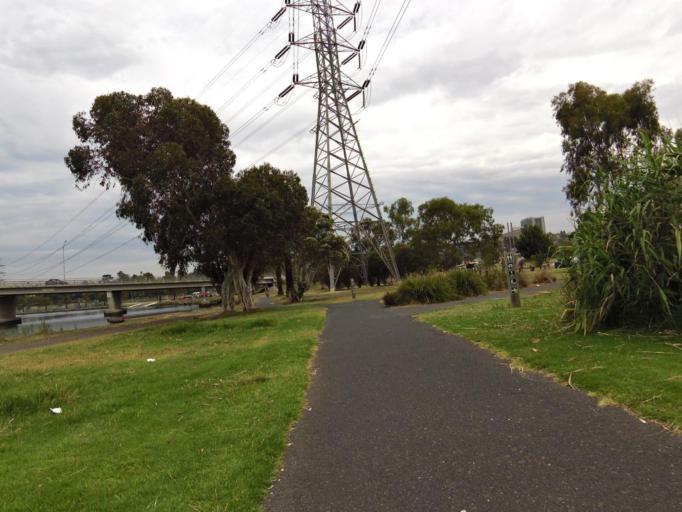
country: AU
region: Victoria
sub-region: Maribyrnong
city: Footscray
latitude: -37.7887
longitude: 144.9025
